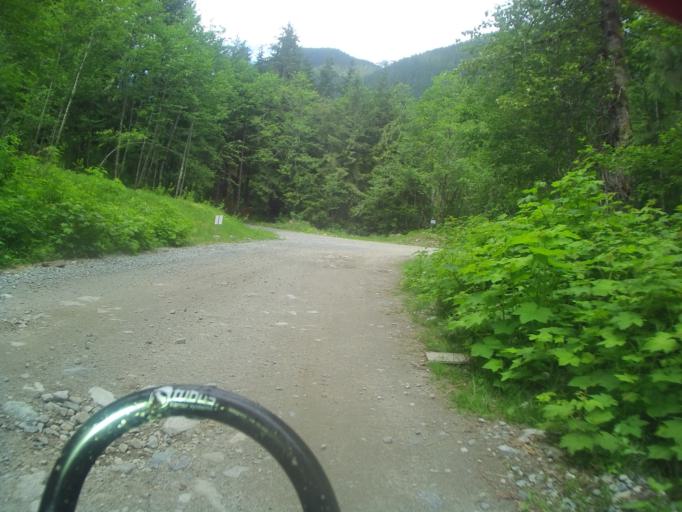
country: CA
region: British Columbia
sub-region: Fraser Valley Regional District
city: Chilliwack
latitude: 49.6893
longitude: -122.1229
